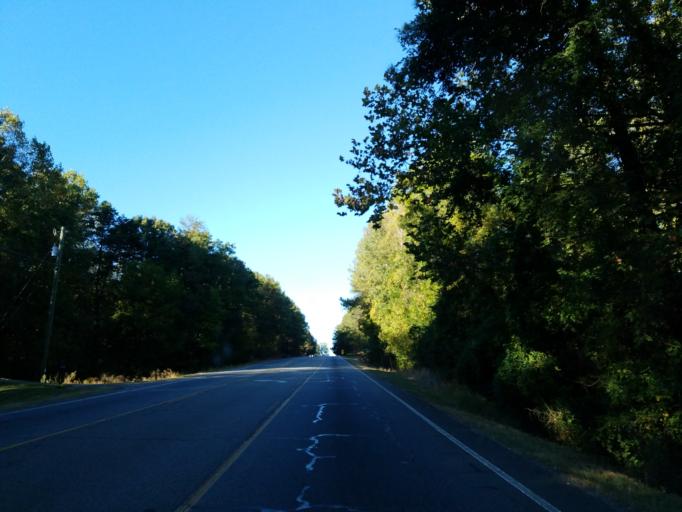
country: US
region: Georgia
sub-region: Cherokee County
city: Ball Ground
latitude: 34.3573
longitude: -84.3784
